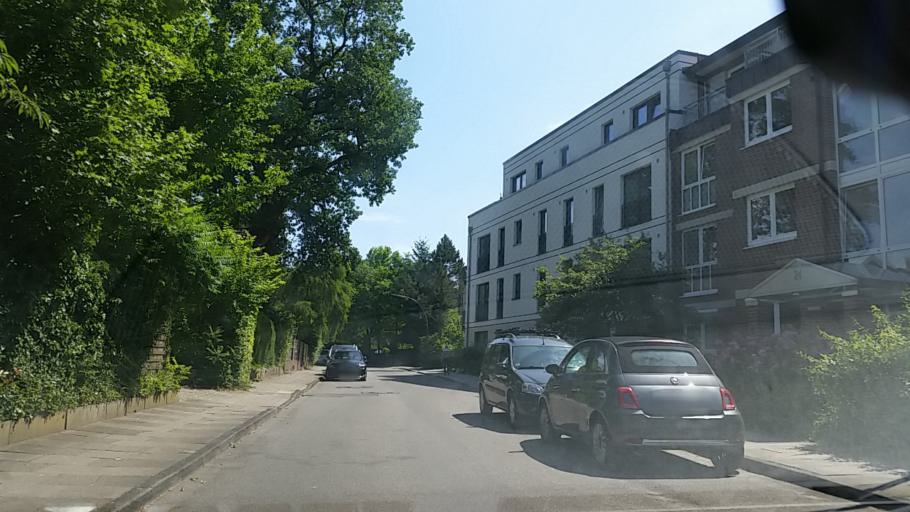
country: DE
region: Schleswig-Holstein
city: Wedel
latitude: 53.5796
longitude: 9.7648
